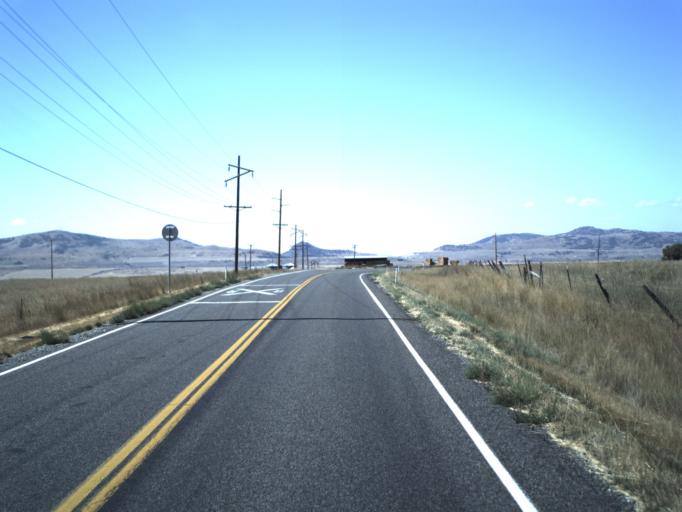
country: US
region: Utah
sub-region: Cache County
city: Benson
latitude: 41.8449
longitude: -111.9614
